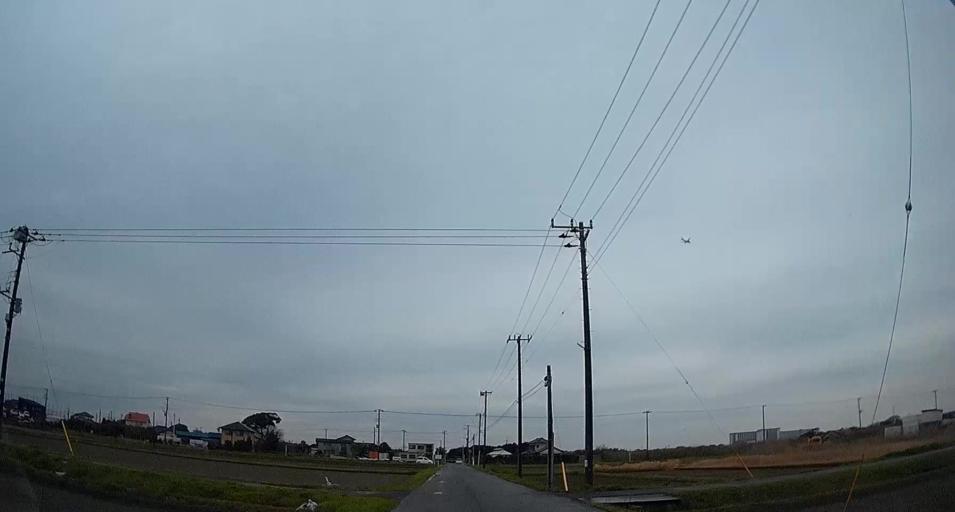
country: JP
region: Chiba
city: Kisarazu
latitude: 35.4134
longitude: 139.9112
